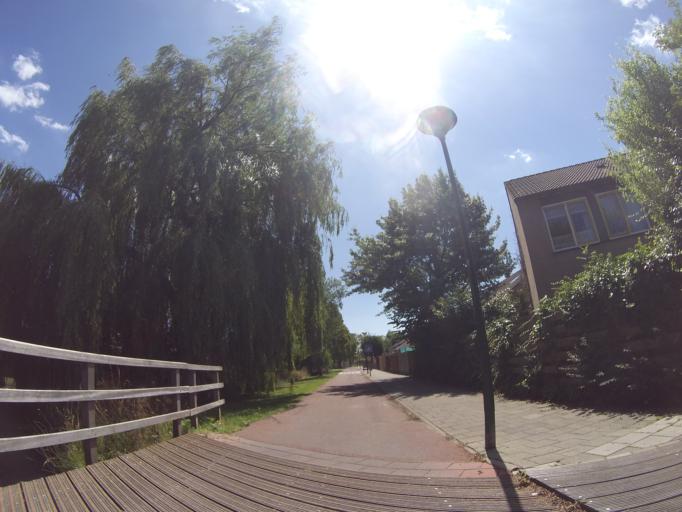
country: NL
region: Utrecht
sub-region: Stichtse Vecht
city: Spechtenkamp
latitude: 52.1397
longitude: 5.0196
